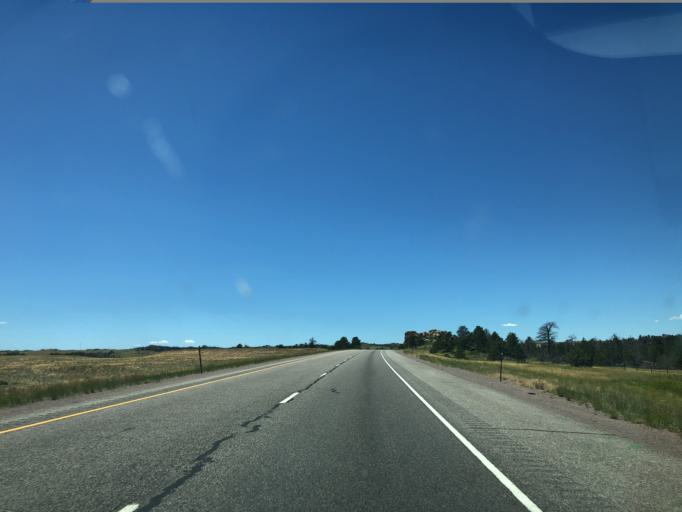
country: US
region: Wyoming
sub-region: Albany County
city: Laramie
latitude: 41.1268
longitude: -105.3266
